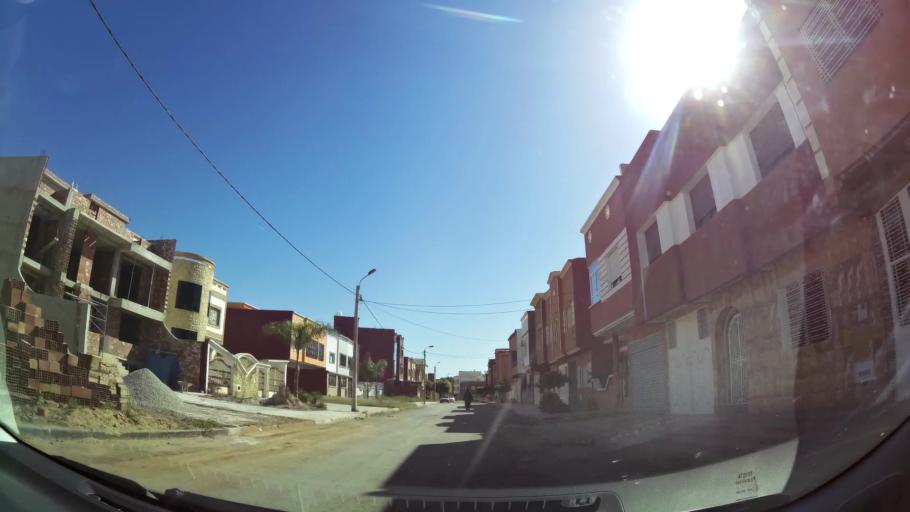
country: MA
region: Oriental
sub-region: Berkane-Taourirt
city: Berkane
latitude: 34.9414
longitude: -2.3393
